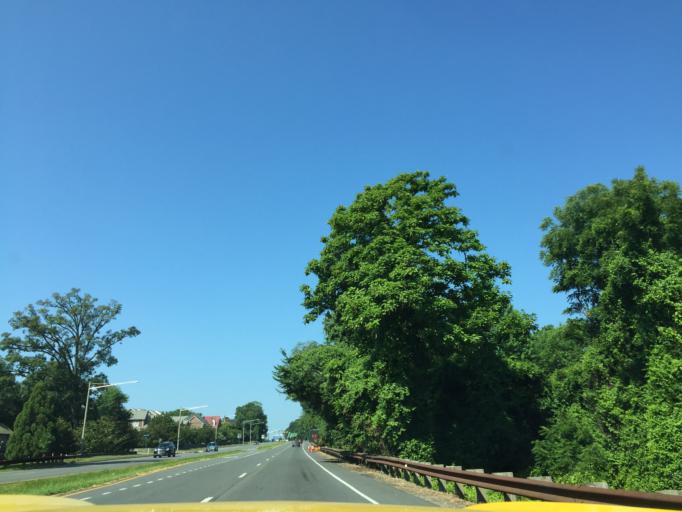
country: US
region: Virginia
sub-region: Fairfax County
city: McLean
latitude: 38.9335
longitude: -77.1941
